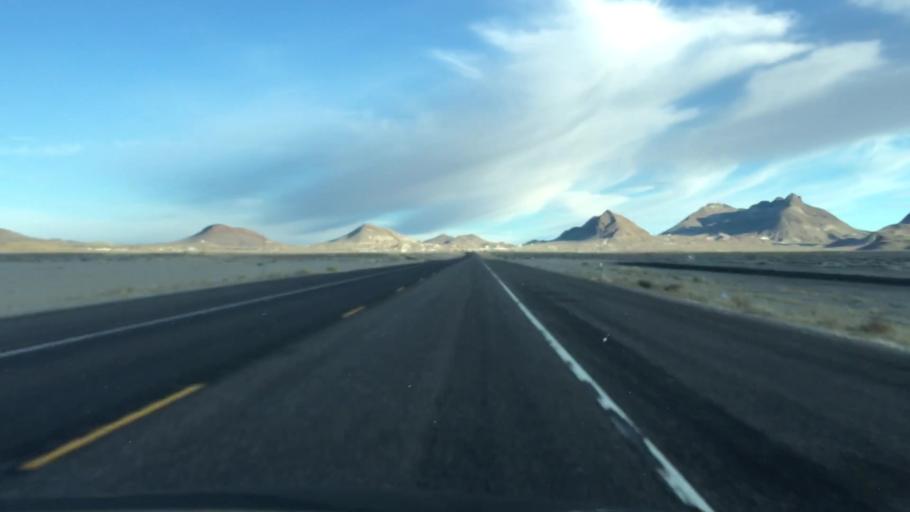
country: US
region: Nevada
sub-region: Nye County
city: Tonopah
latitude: 38.0862
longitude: -117.2850
